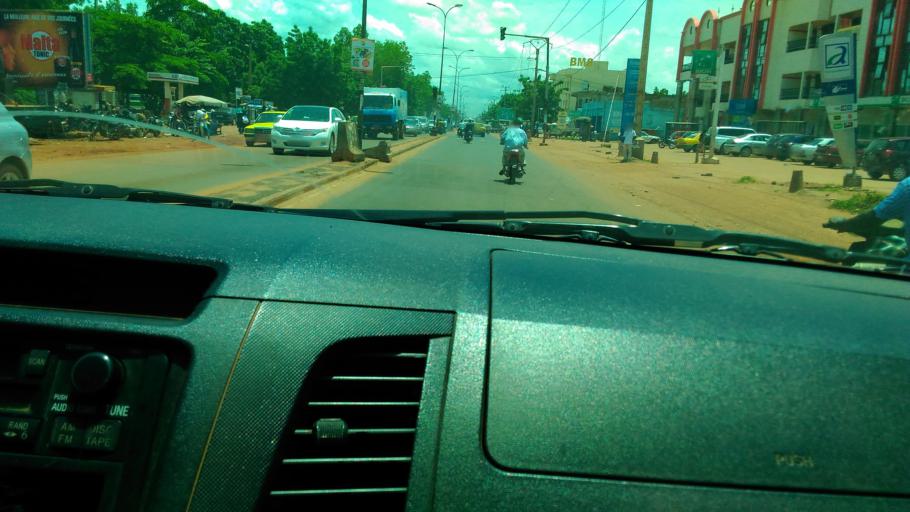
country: ML
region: Bamako
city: Bamako
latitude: 12.6641
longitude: -7.9421
